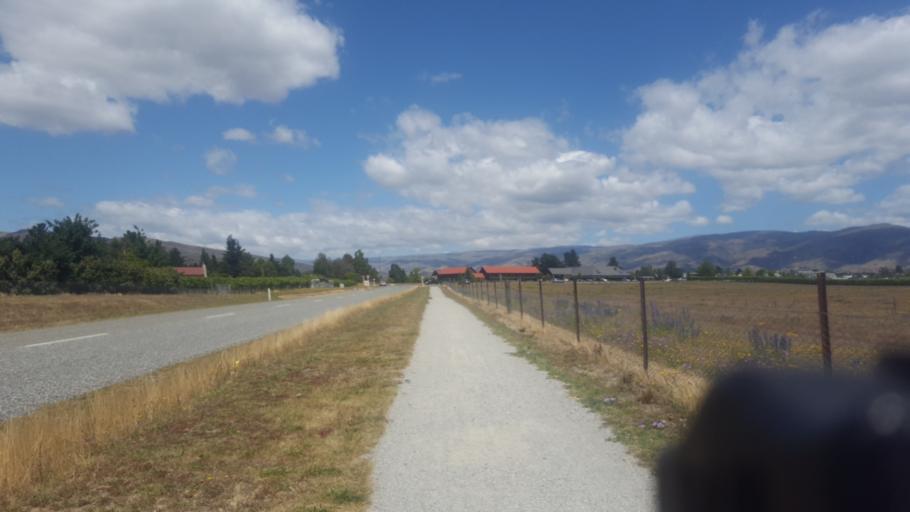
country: NZ
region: Otago
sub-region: Queenstown-Lakes District
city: Wanaka
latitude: -45.0326
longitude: 169.2028
